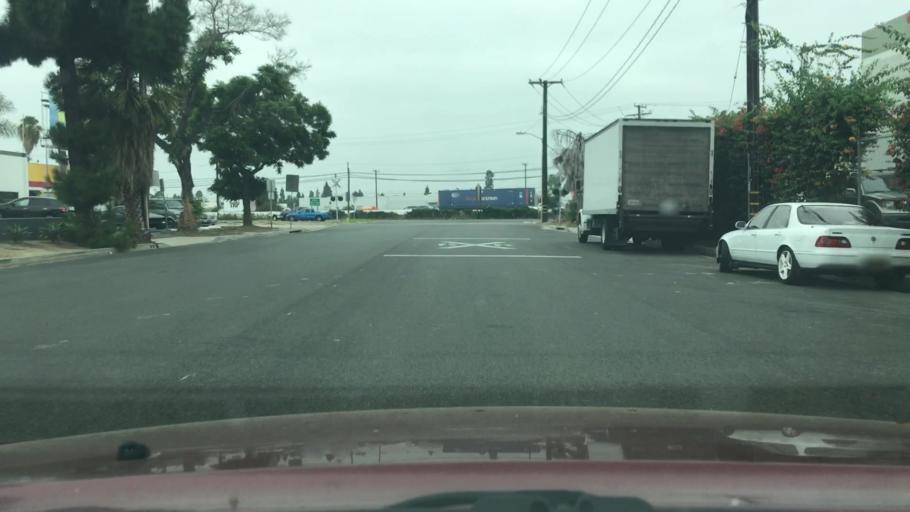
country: US
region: California
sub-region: Orange County
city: Buena Park
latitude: 33.8815
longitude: -118.0216
